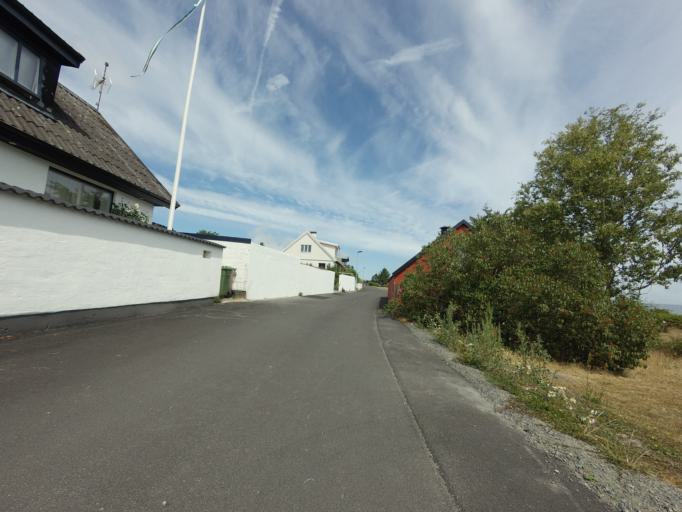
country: SE
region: Skane
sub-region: Simrishamns Kommun
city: Simrishamn
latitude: 55.5439
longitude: 14.3571
